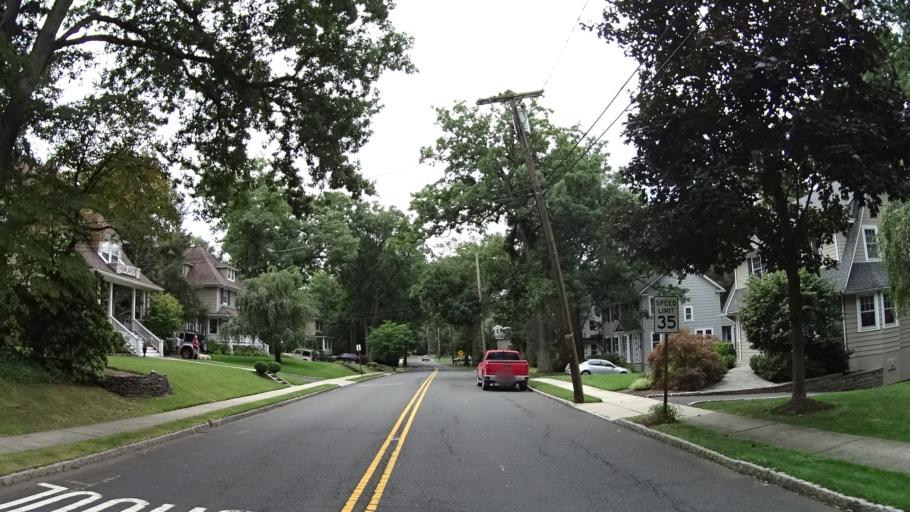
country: US
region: New Jersey
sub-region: Union County
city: Summit
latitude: 40.7072
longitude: -74.3618
